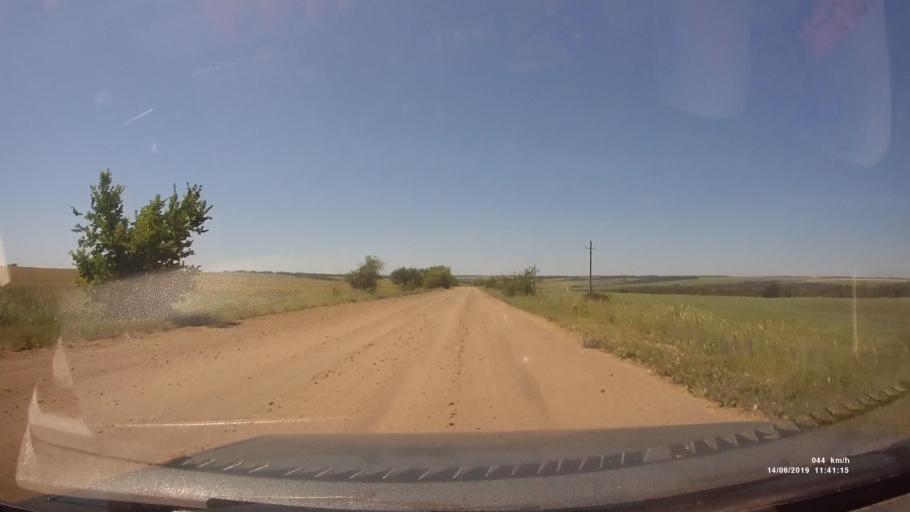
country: RU
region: Rostov
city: Kazanskaya
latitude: 49.8643
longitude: 41.3544
